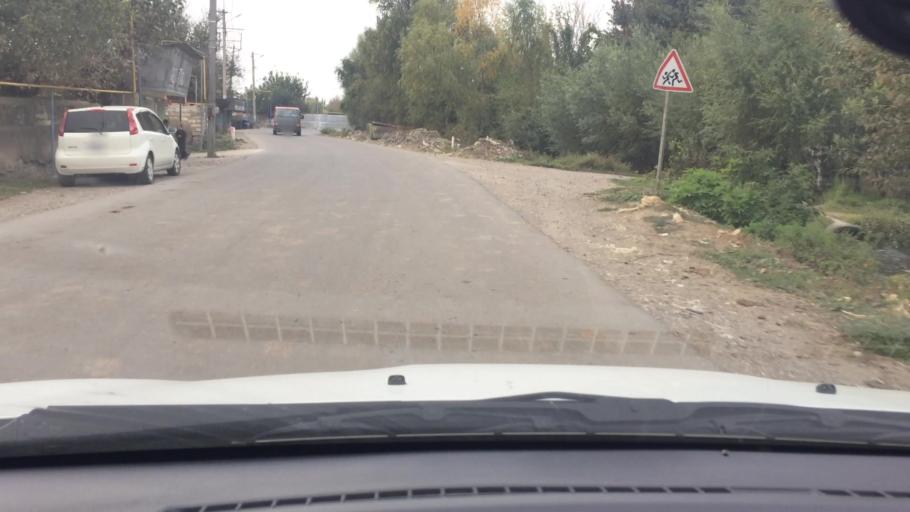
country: AM
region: Tavush
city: Berdavan
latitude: 41.3508
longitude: 44.9713
